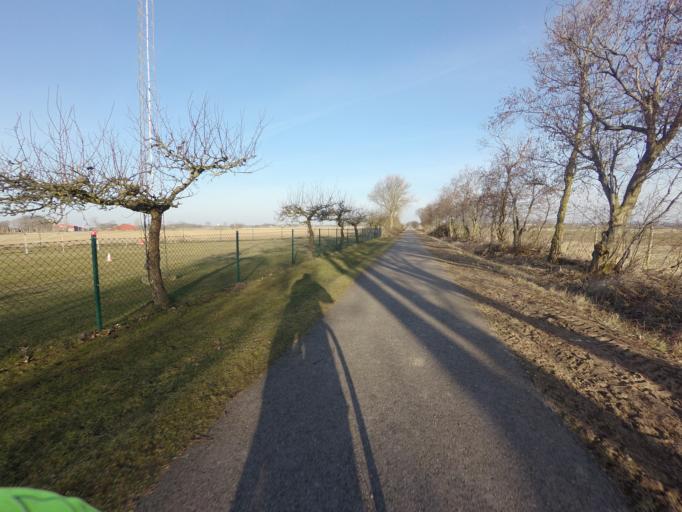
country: SE
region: Skane
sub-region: Hoganas Kommun
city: Hoganas
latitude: 56.1886
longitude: 12.6252
